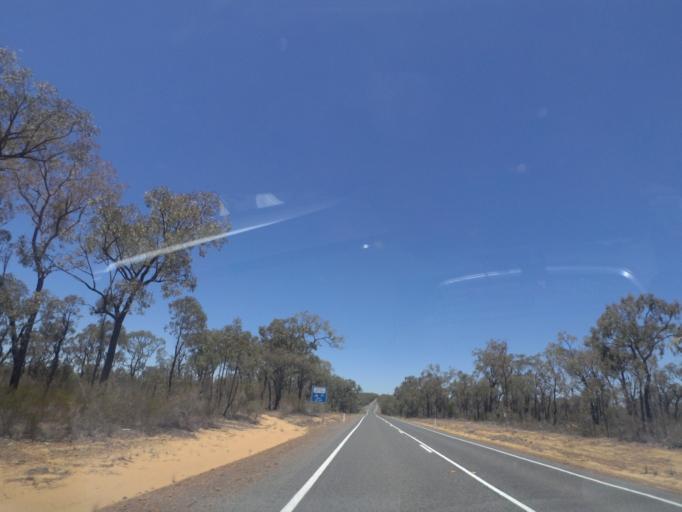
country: AU
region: New South Wales
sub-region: Narrabri
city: Narrabri
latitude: -30.7177
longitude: 149.5269
